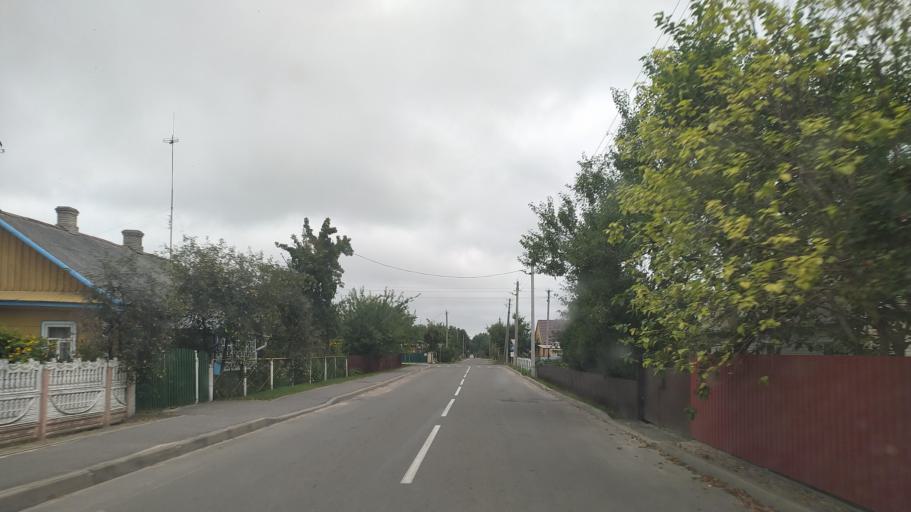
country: BY
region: Brest
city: Byaroza
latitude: 52.5319
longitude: 24.9686
